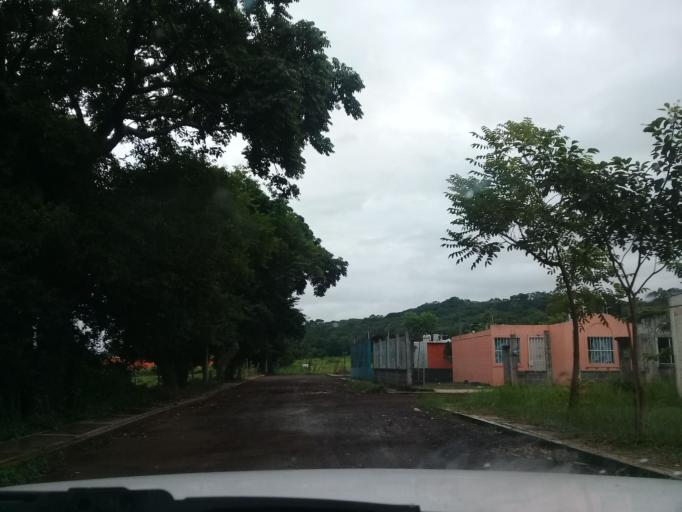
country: MX
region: Veracruz
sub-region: San Andres Tuxtla
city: Texalpan de Arriba
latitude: 18.4253
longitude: -95.2217
